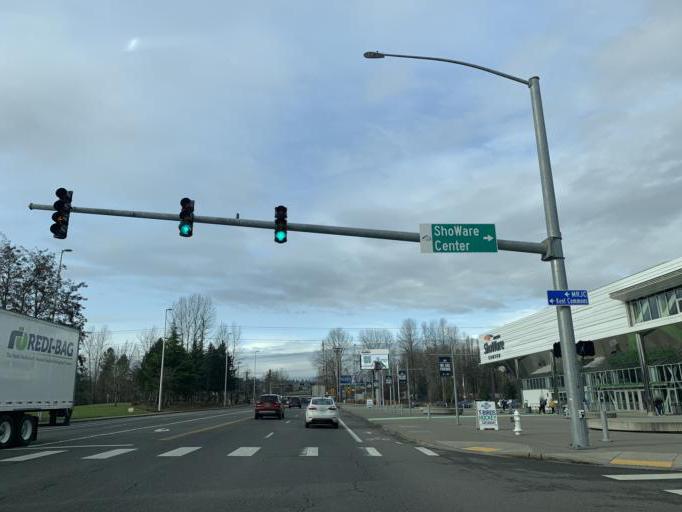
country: US
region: Washington
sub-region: King County
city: Kent
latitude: 47.3867
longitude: -122.2392
